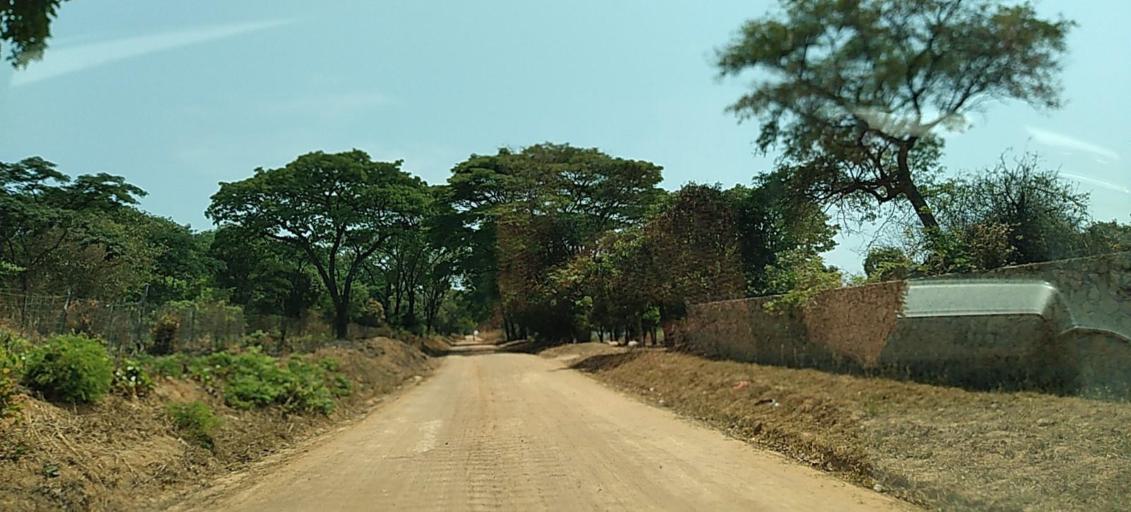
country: ZM
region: Copperbelt
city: Chingola
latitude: -12.6028
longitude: 27.9548
